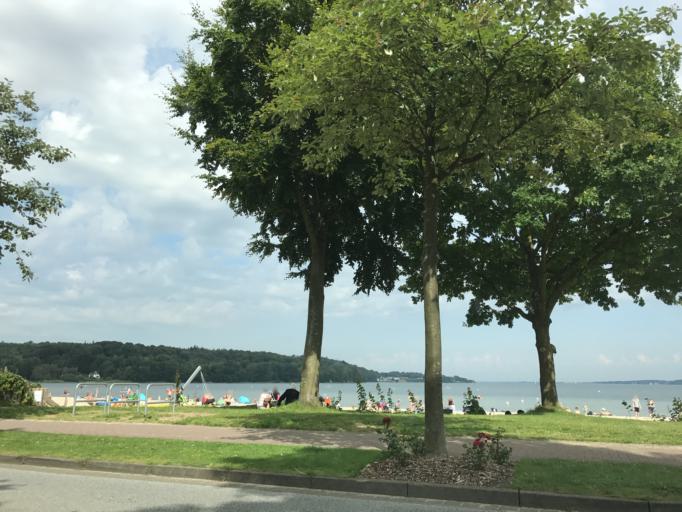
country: DK
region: South Denmark
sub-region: Aabenraa Kommune
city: Krusa
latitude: 54.8259
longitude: 9.4195
